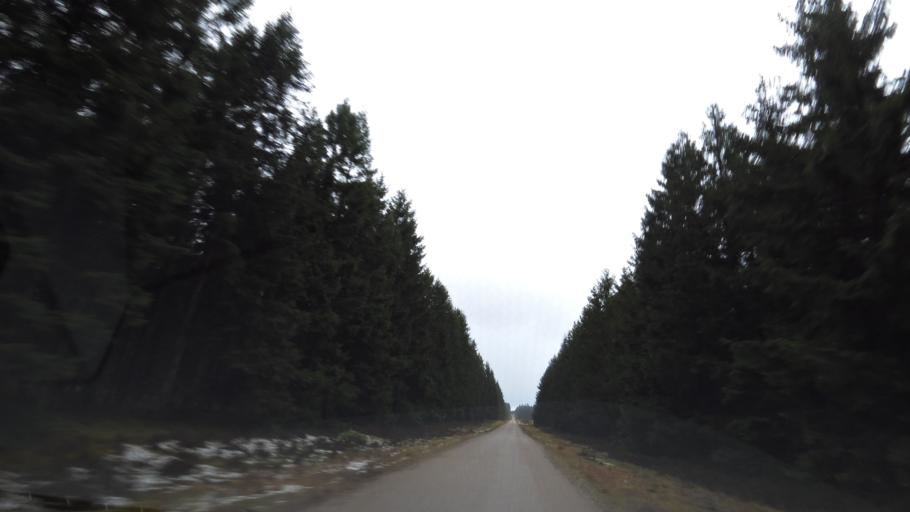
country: DK
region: Central Jutland
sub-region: Ikast-Brande Kommune
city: Brande
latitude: 56.0081
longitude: 9.1659
